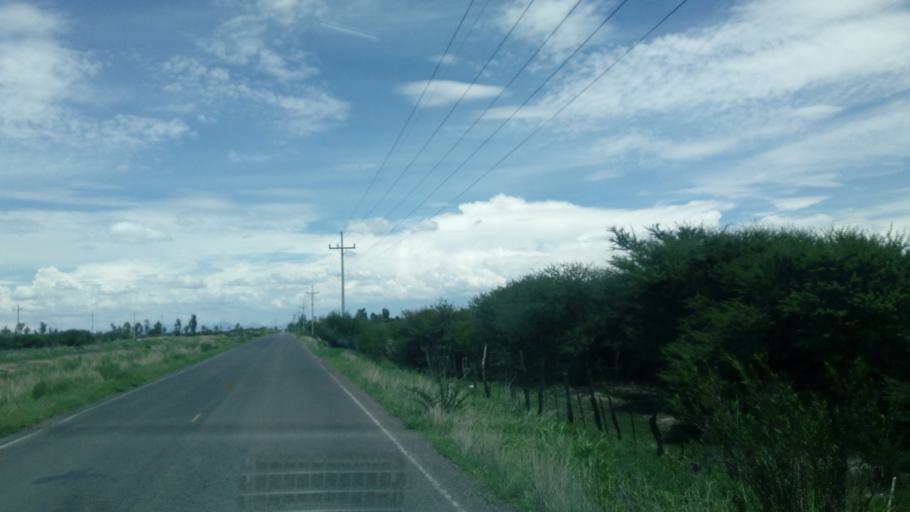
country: MX
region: Durango
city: Victoria de Durango
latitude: 24.1343
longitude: -104.5428
